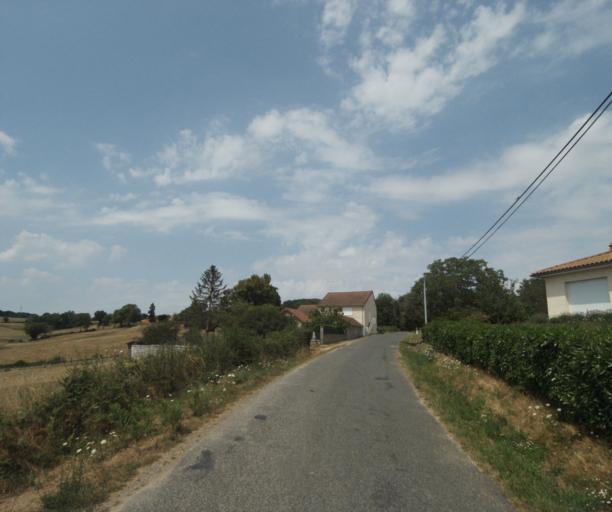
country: FR
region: Bourgogne
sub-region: Departement de Saone-et-Loire
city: Gueugnon
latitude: 46.6012
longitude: 4.0118
